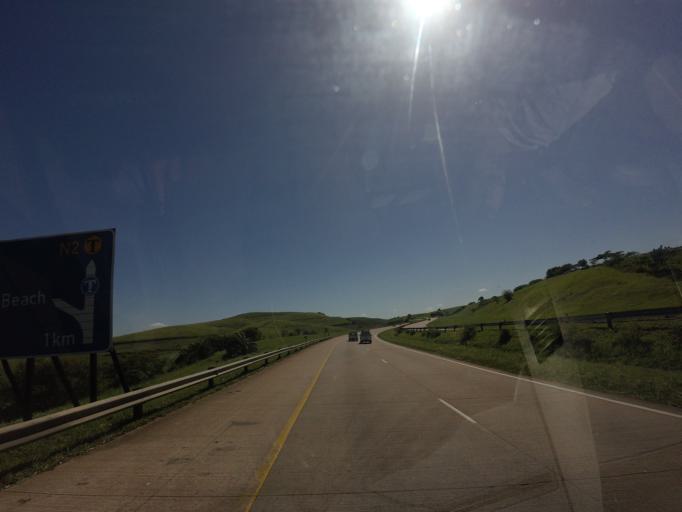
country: ZA
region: KwaZulu-Natal
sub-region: iLembe District Municipality
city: Ballitoville
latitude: -29.4396
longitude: 31.2613
